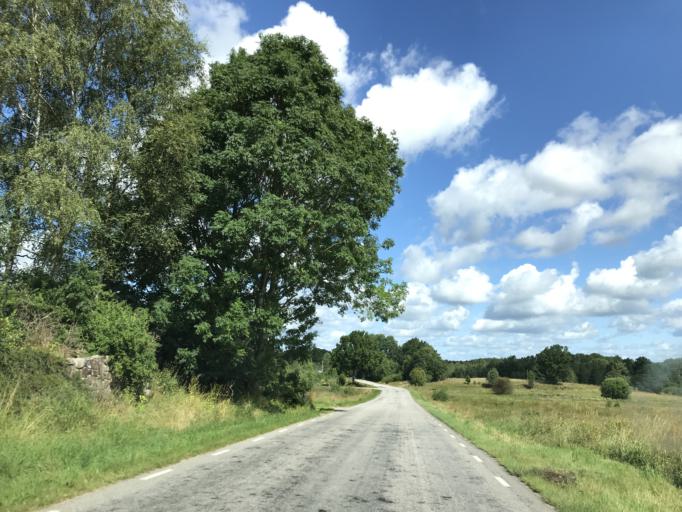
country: SE
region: Halland
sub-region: Laholms Kommun
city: Knared
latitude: 56.4628
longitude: 13.3250
